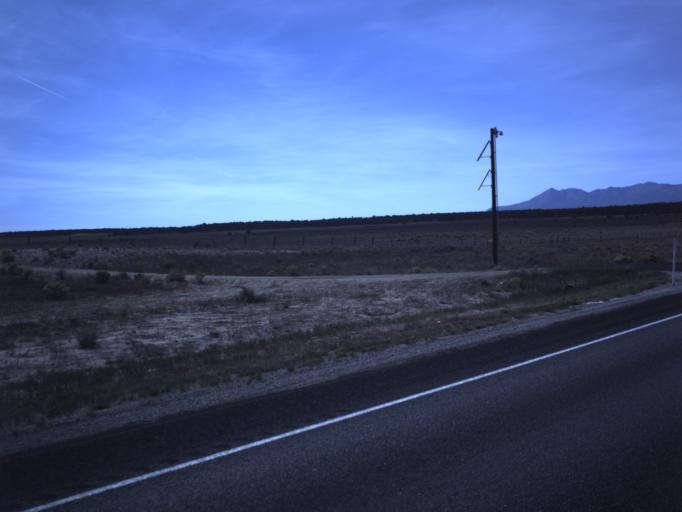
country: US
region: Colorado
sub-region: Dolores County
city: Dove Creek
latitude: 37.8329
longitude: -109.0991
